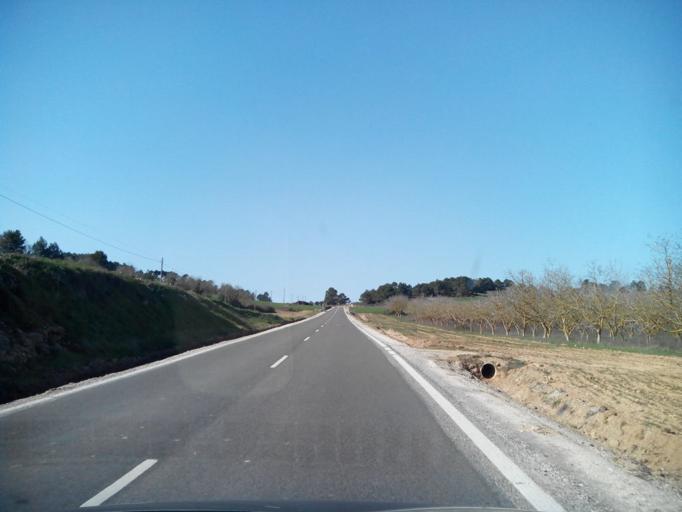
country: ES
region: Catalonia
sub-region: Provincia de Tarragona
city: Conesa
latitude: 41.4949
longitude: 1.3261
